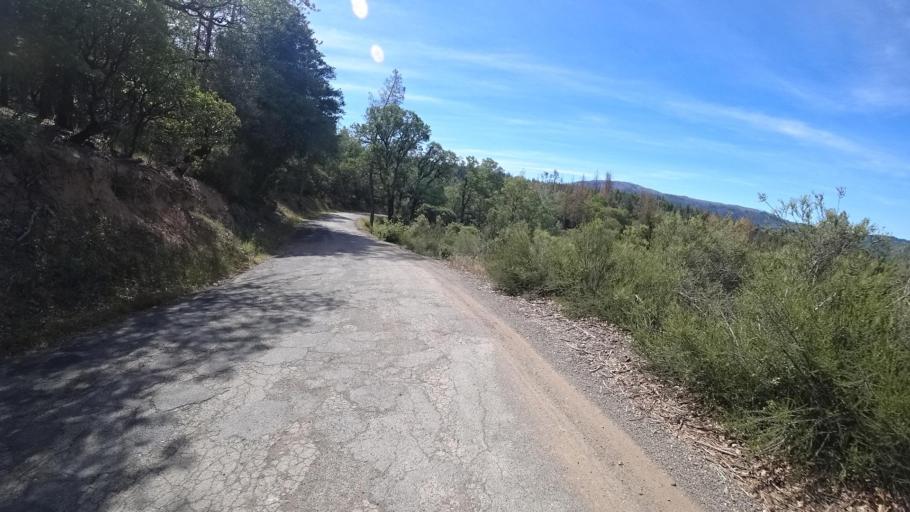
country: US
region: California
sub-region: Lake County
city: Cobb
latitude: 38.8646
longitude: -122.7441
